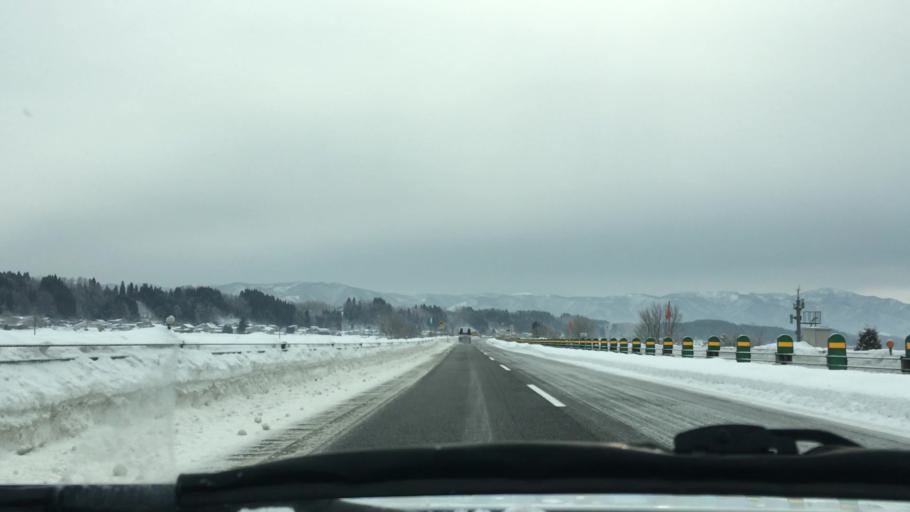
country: JP
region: Akita
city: Hanawa
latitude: 40.3004
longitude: 140.7471
